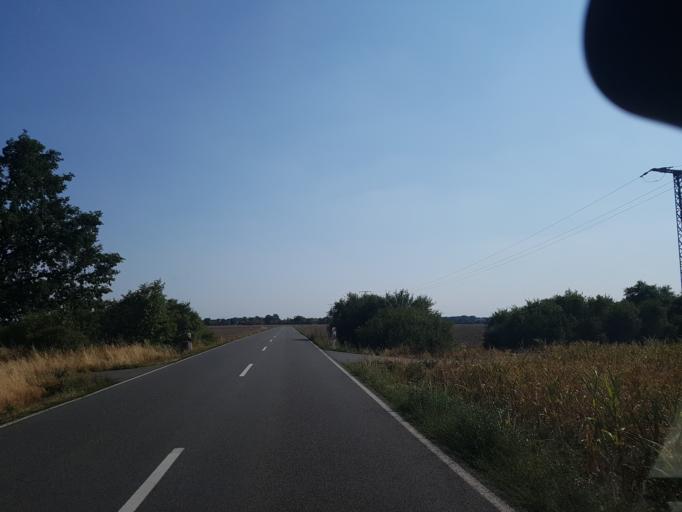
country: DE
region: Saxony-Anhalt
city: Annaburg
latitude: 51.6854
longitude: 12.9968
